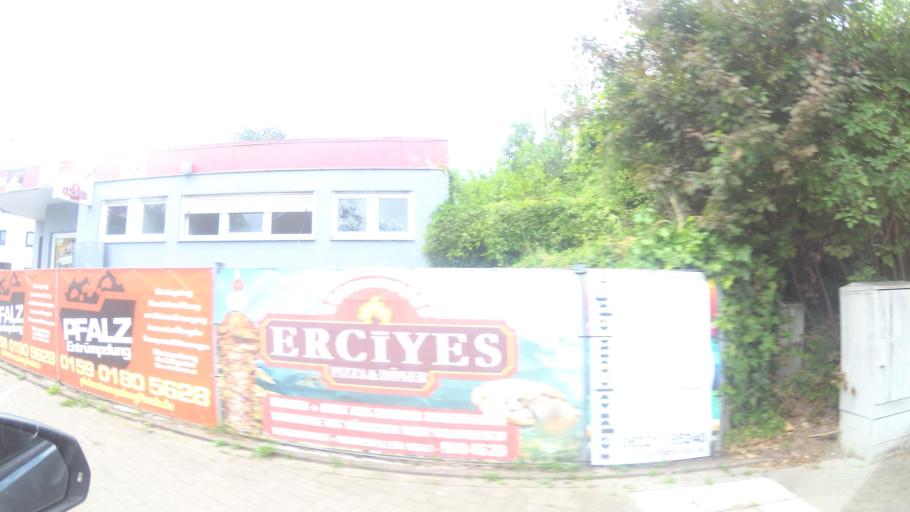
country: DE
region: Rheinland-Pfalz
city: Neustadt
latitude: 49.3519
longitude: 8.1565
